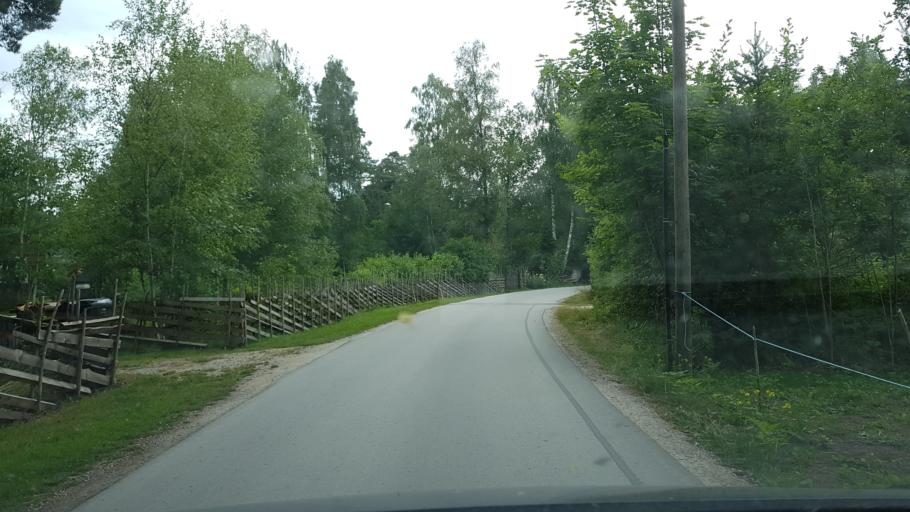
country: SE
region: Gotland
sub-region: Gotland
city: Hemse
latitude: 57.3378
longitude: 18.7080
